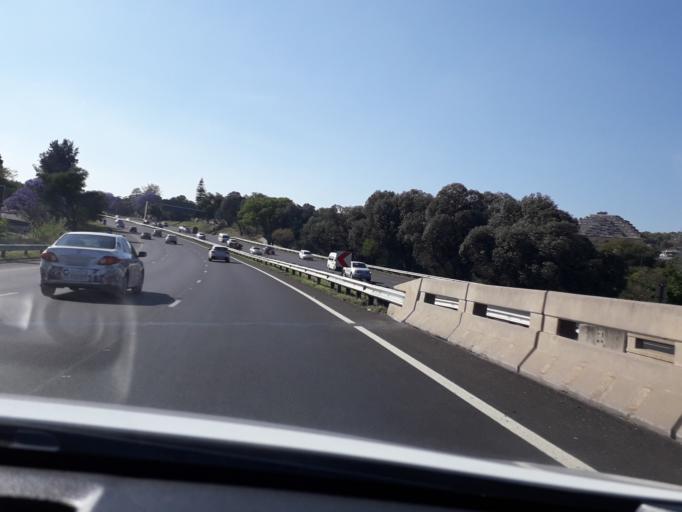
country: ZA
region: Gauteng
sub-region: City of Tshwane Metropolitan Municipality
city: Pretoria
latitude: -25.7503
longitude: 28.2966
